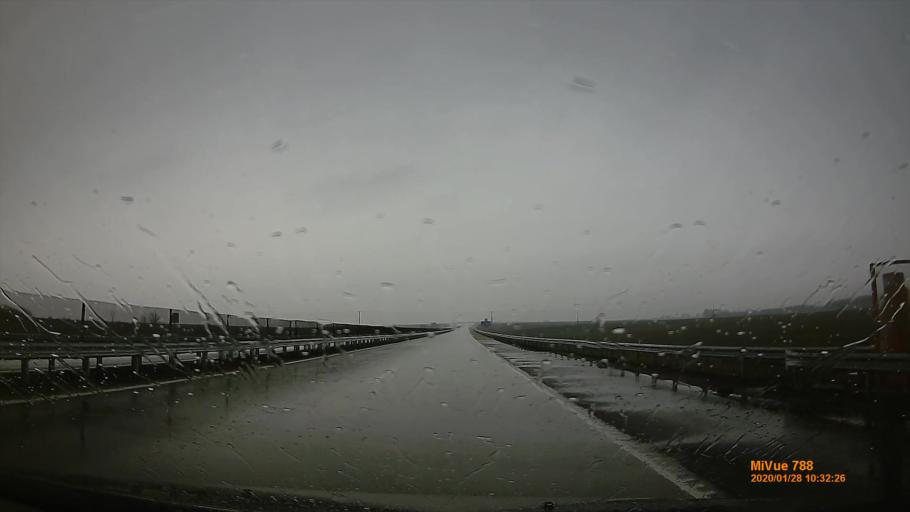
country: HU
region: Pest
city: Gomba
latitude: 47.3492
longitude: 19.4931
